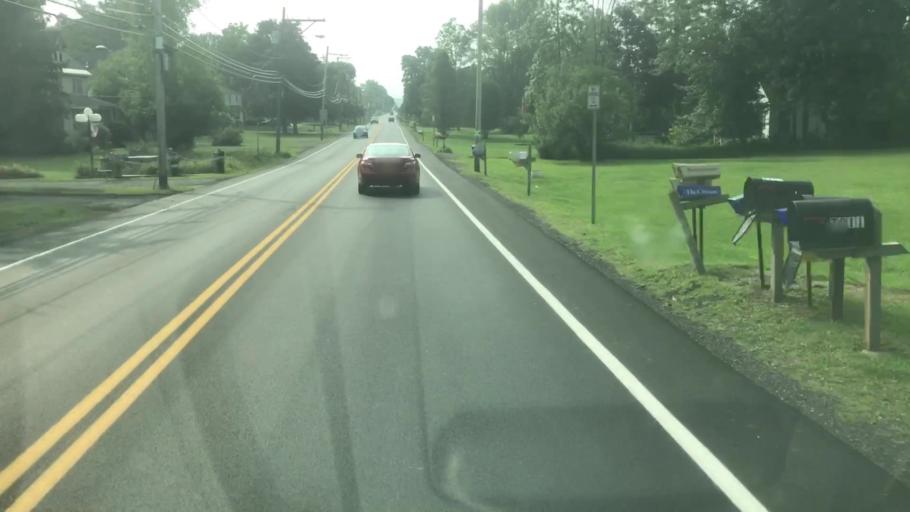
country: US
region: New York
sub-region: Cayuga County
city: Melrose Park
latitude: 42.9097
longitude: -76.5410
